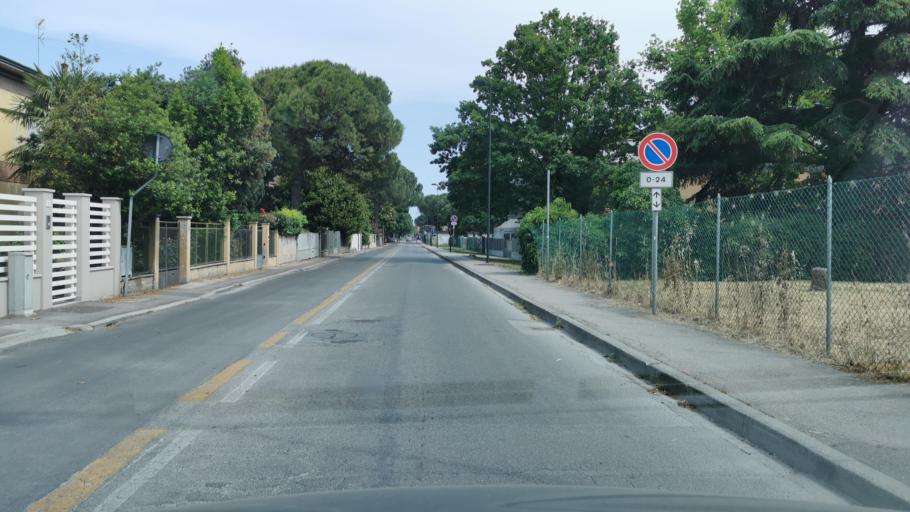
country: IT
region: Emilia-Romagna
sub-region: Provincia di Ravenna
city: Ravenna
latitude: 44.4135
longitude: 12.1876
